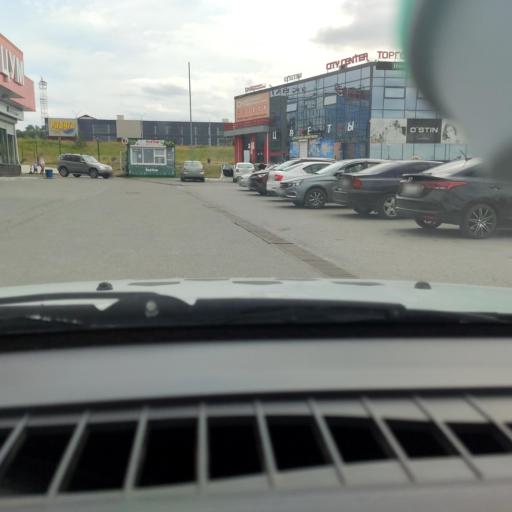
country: RU
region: Perm
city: Solikamsk
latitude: 59.6485
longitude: 56.7722
